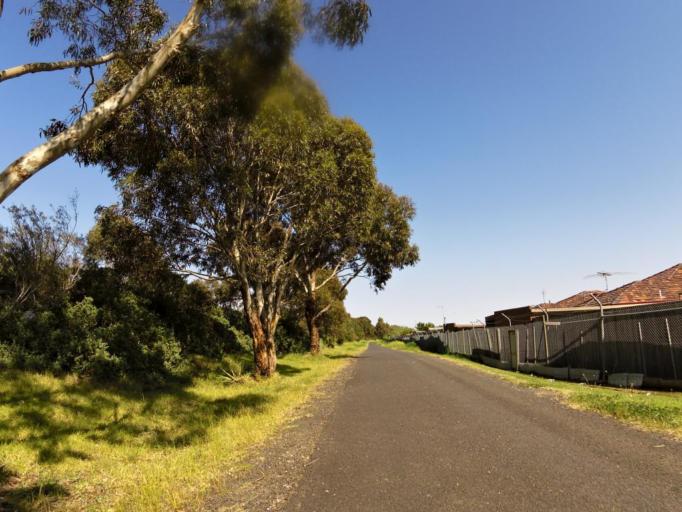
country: AU
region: Victoria
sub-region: Whittlesea
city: Thomastown
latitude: -37.6870
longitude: 144.9997
